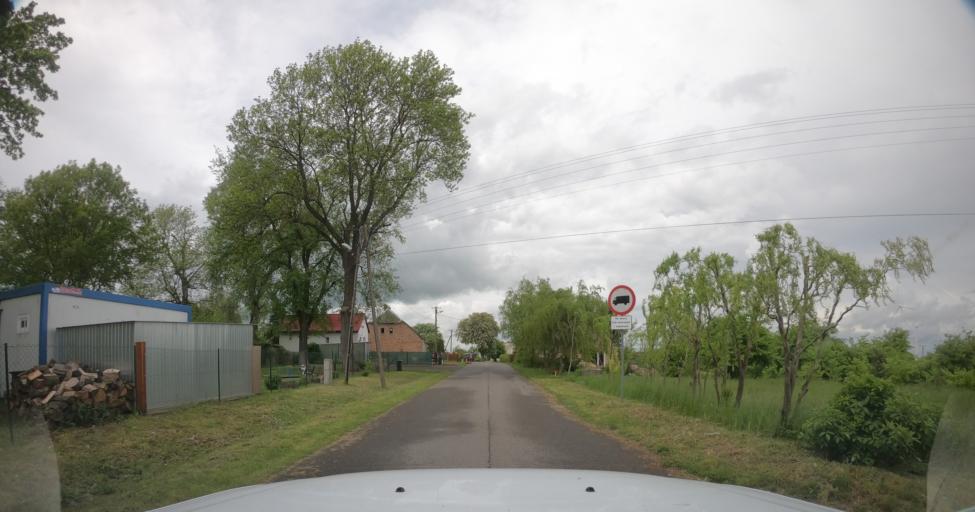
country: PL
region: West Pomeranian Voivodeship
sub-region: Powiat pyrzycki
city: Kozielice
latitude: 53.0821
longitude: 14.8384
